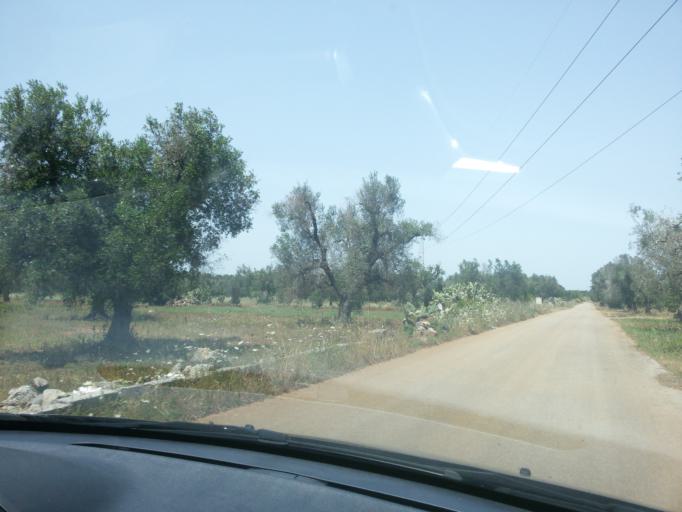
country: IT
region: Apulia
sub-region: Provincia di Lecce
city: Porto Cesareo
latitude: 40.3207
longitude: 17.8939
